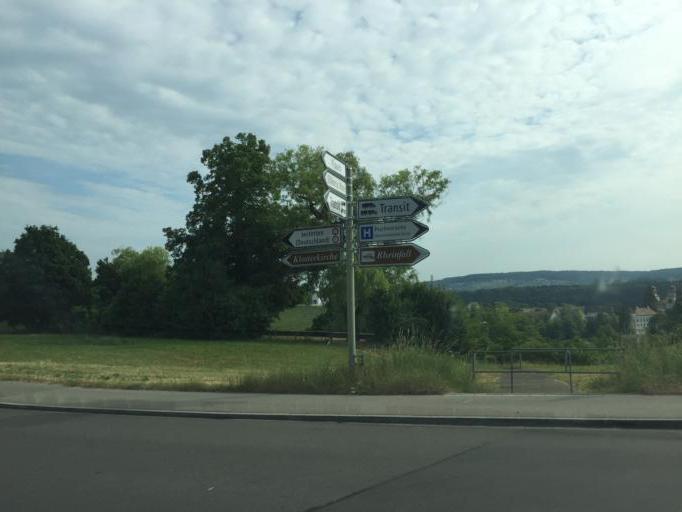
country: CH
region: Zurich
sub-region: Bezirk Andelfingen
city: Dachsen
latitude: 47.6381
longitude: 8.6004
